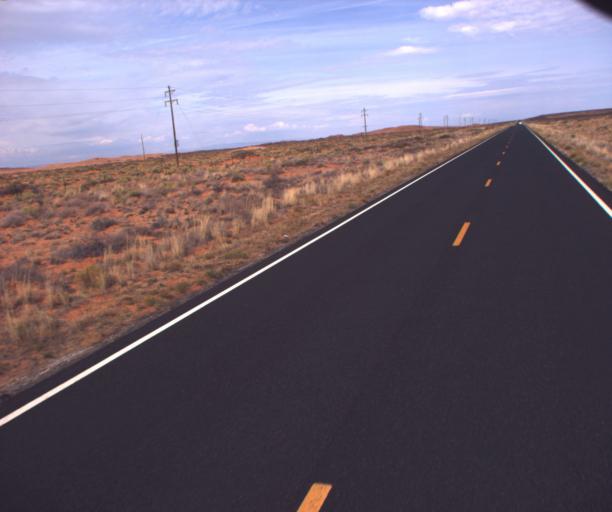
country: US
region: Arizona
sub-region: Apache County
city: Many Farms
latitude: 36.8618
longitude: -109.6350
